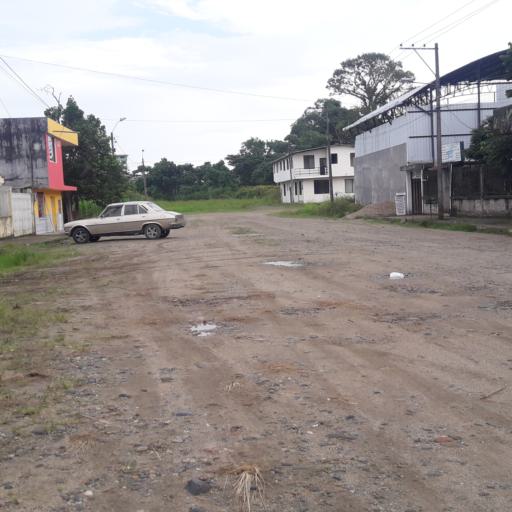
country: EC
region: Napo
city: Tena
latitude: -0.9901
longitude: -77.8106
